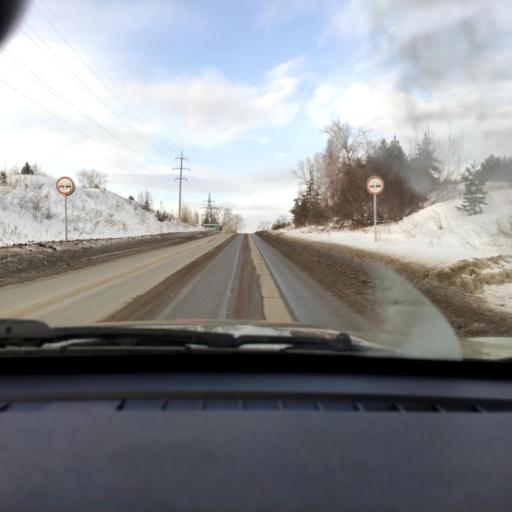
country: RU
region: Samara
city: Pribrezhnyy
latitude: 53.4933
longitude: 49.8474
